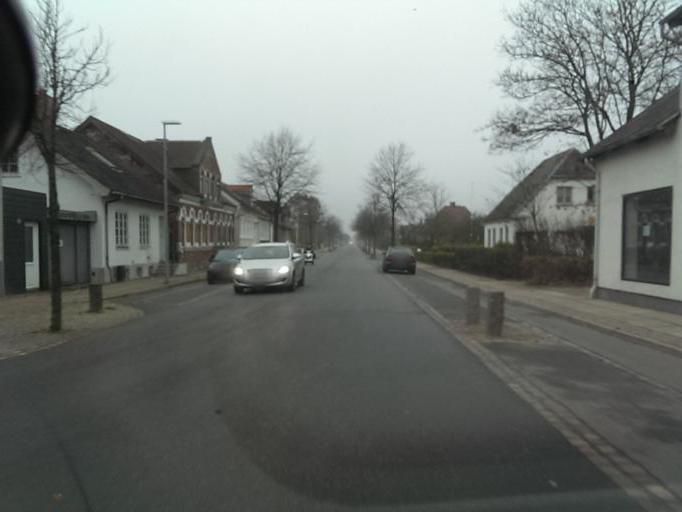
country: DK
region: South Denmark
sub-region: Esbjerg Kommune
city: Bramming
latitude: 55.4657
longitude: 8.6962
